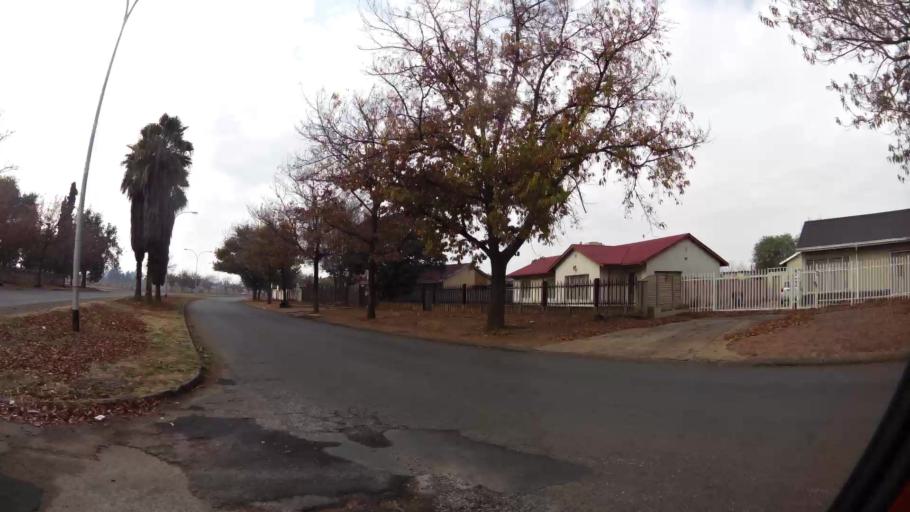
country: ZA
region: Gauteng
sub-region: Sedibeng District Municipality
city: Vanderbijlpark
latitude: -26.6960
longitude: 27.8513
